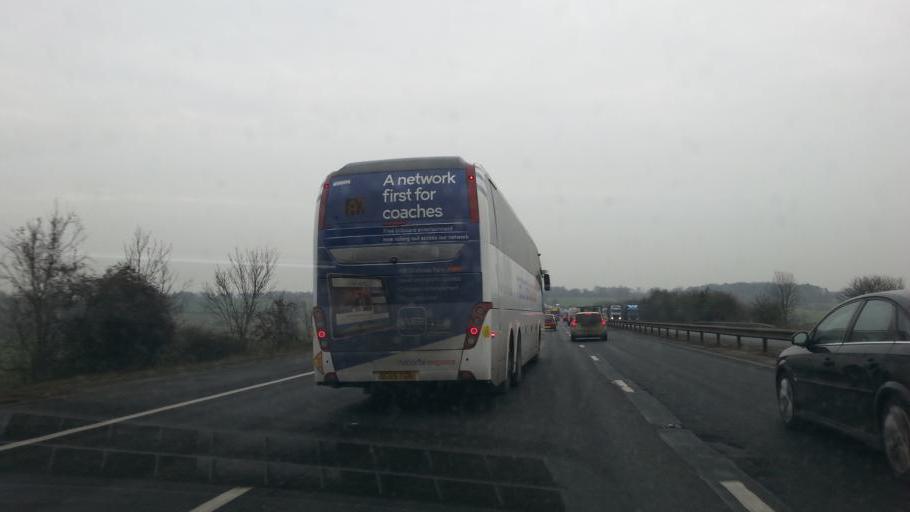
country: GB
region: England
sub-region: Hertfordshire
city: Sawbridgeworth
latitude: 51.7907
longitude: 0.1715
